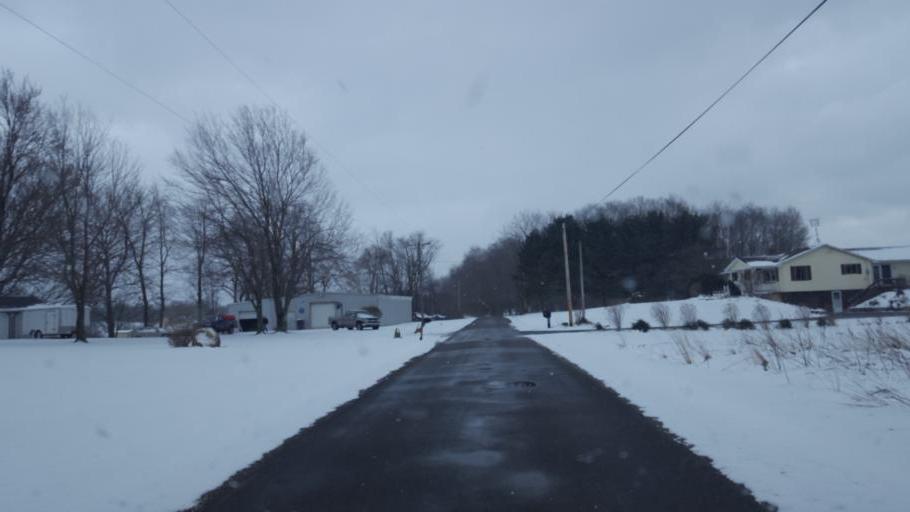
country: US
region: Pennsylvania
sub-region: Mercer County
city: Stoneboro
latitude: 41.4018
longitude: -80.0872
